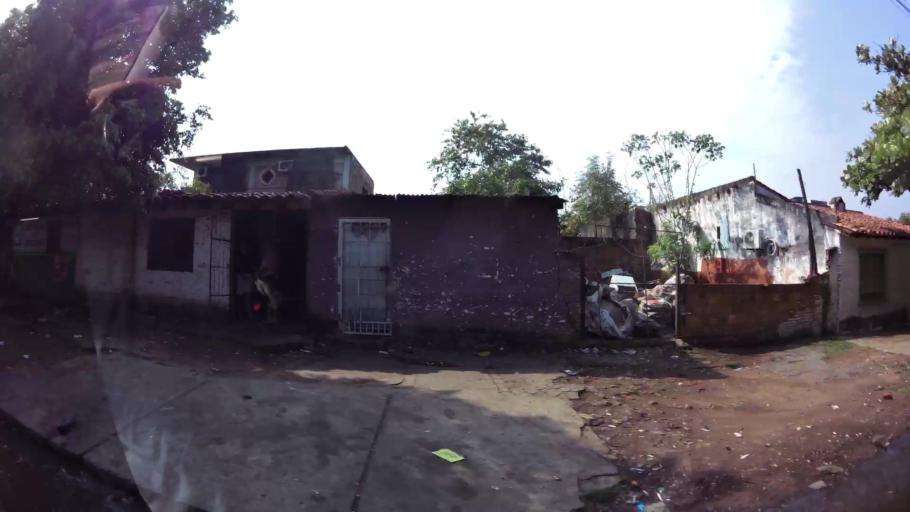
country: PY
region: Asuncion
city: Asuncion
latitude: -25.2971
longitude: -57.6614
